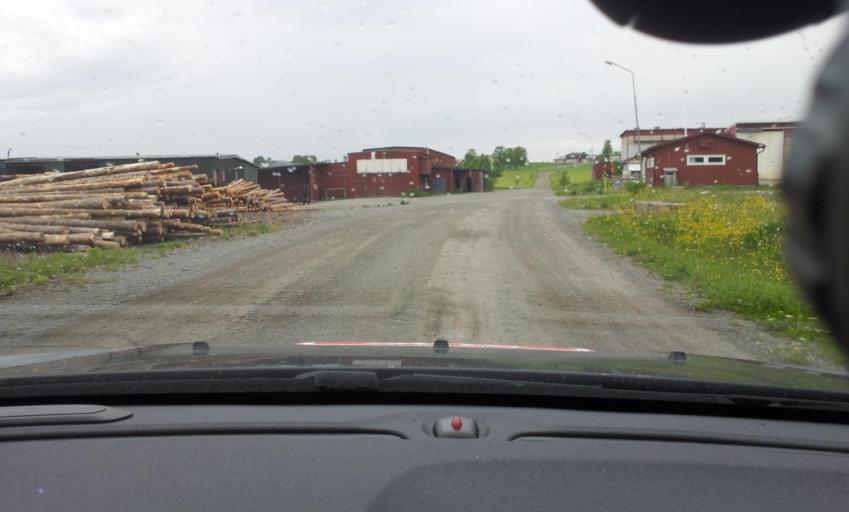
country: SE
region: Jaemtland
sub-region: OEstersunds Kommun
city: Ostersund
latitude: 62.9832
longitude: 14.5863
